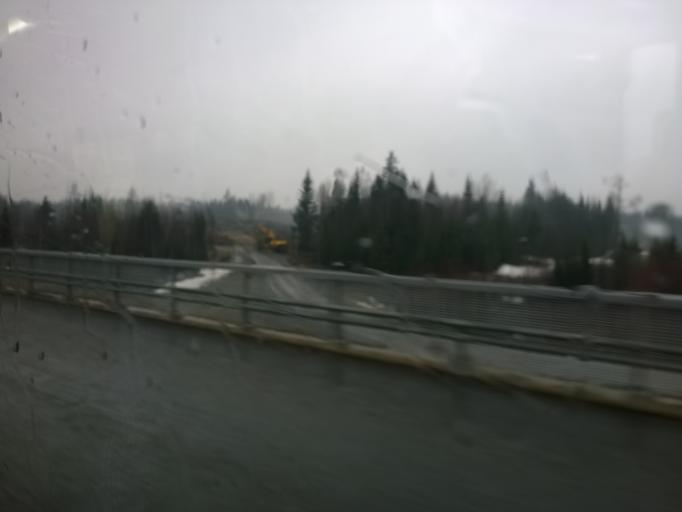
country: FI
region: Pirkanmaa
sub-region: Tampere
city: Tampere
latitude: 61.4354
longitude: 23.8097
